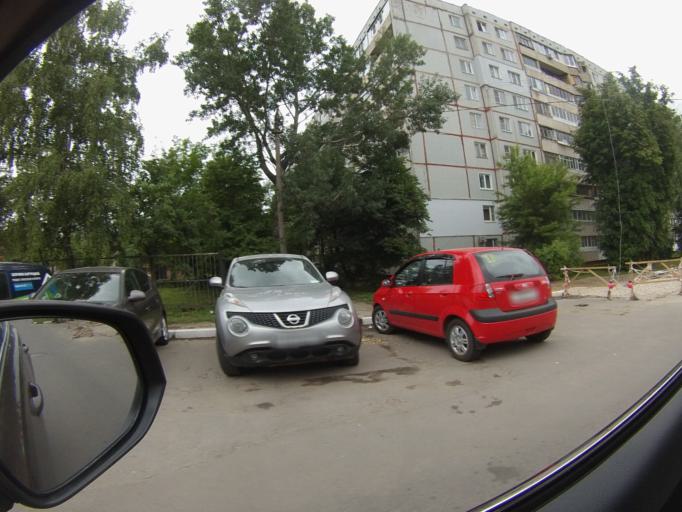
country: RU
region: Tula
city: Tula
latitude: 54.1934
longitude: 37.5990
